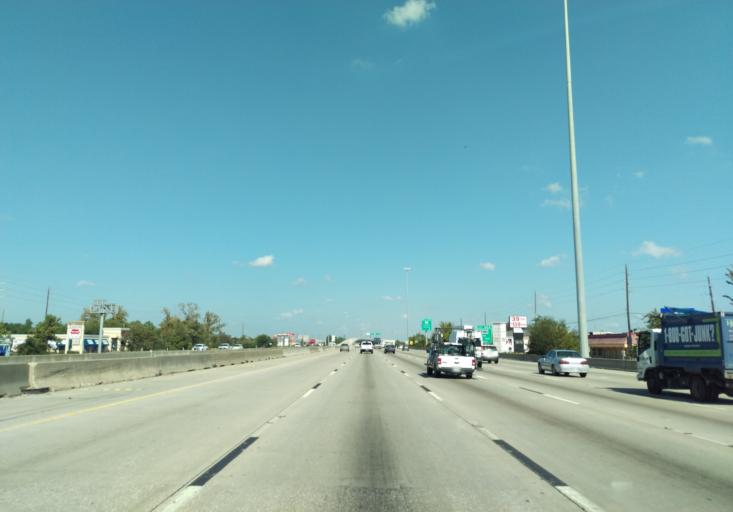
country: US
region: Texas
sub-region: Harris County
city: Spring
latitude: 30.0052
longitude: -95.4268
